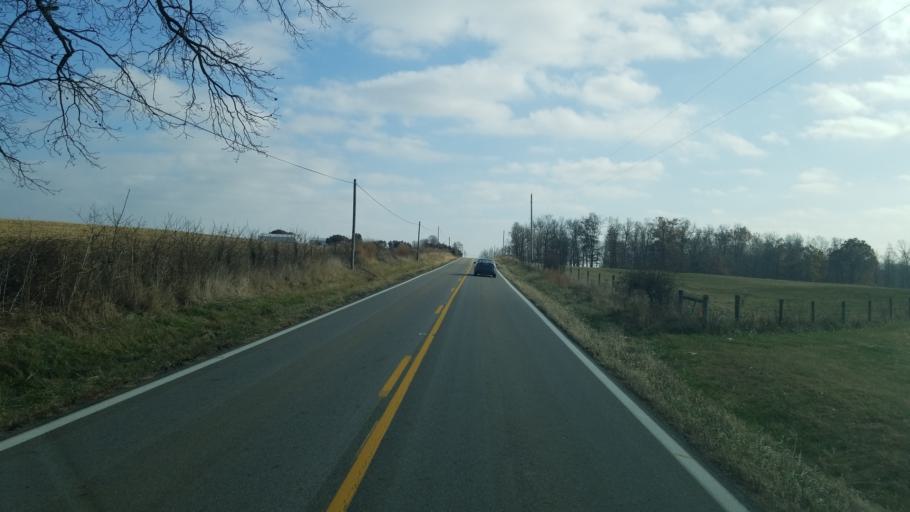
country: US
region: Ohio
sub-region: Licking County
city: Utica
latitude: 40.1818
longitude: -82.5084
